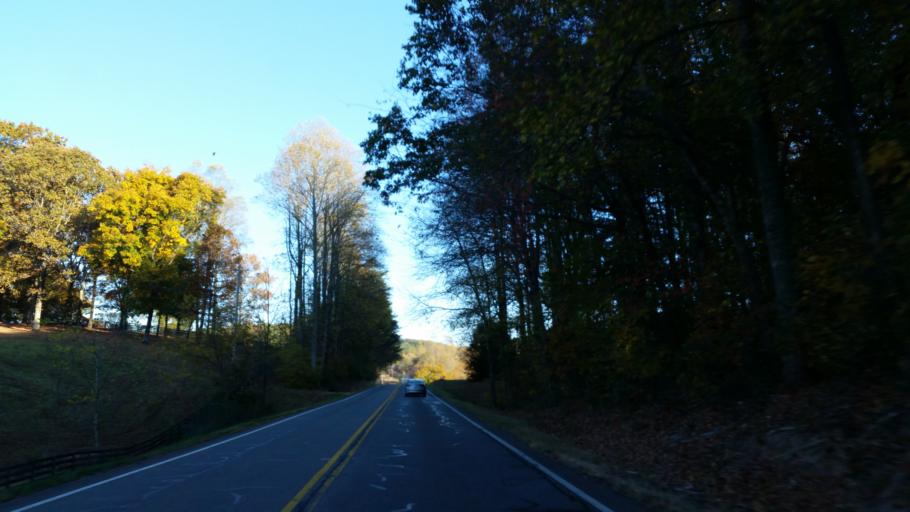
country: US
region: Georgia
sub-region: Pickens County
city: Jasper
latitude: 34.6023
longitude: -84.3438
